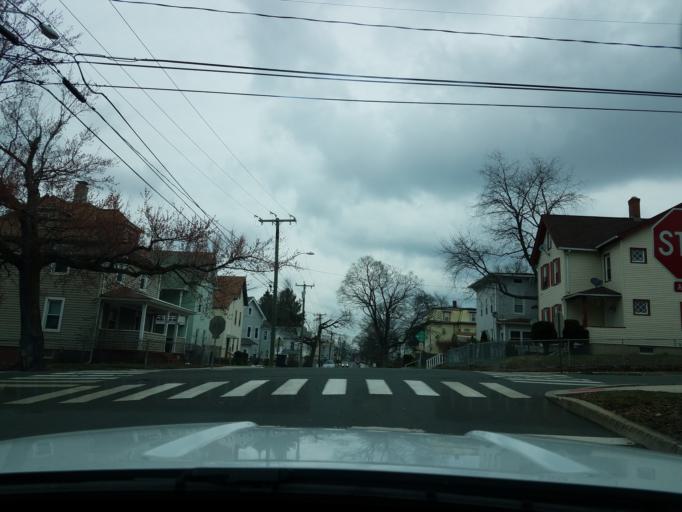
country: US
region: Connecticut
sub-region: Hartford County
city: New Britain
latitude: 41.6566
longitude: -72.7813
